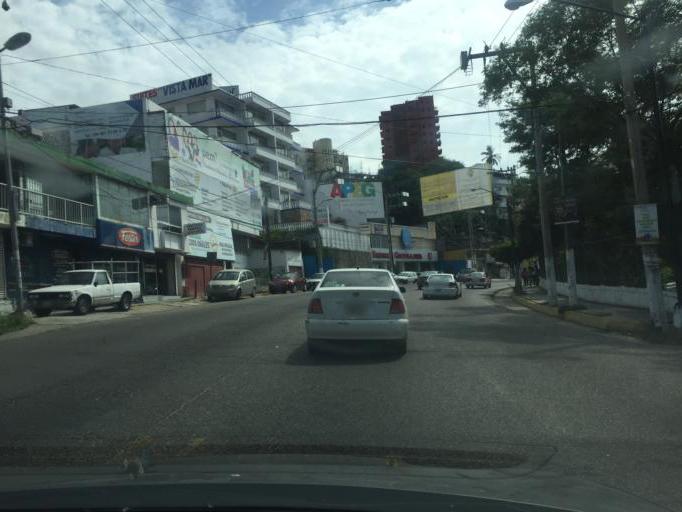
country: MX
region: Guerrero
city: Acapulco de Juarez
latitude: 16.8627
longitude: -99.8691
